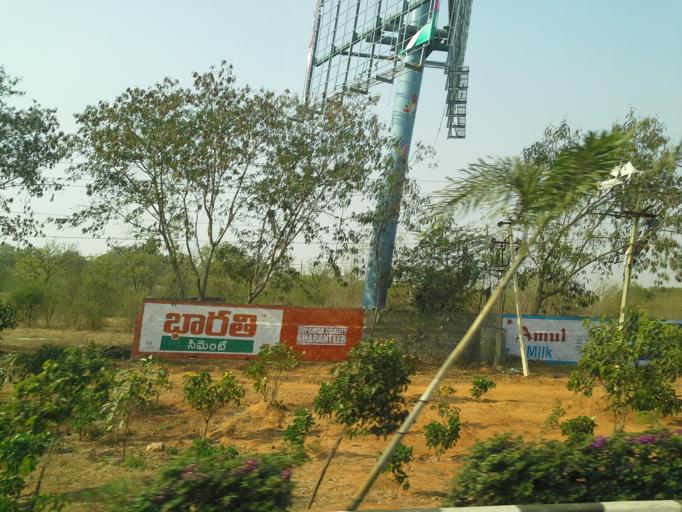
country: IN
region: Telangana
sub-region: Rangareddi
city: Balapur
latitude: 17.2765
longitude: 78.4033
